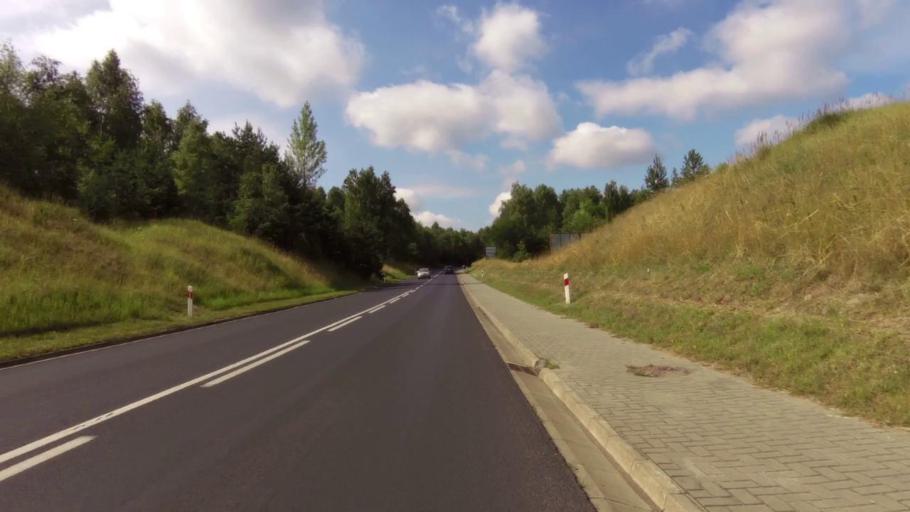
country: PL
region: West Pomeranian Voivodeship
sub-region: Powiat gryfinski
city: Cedynia
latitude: 52.8470
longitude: 14.1394
